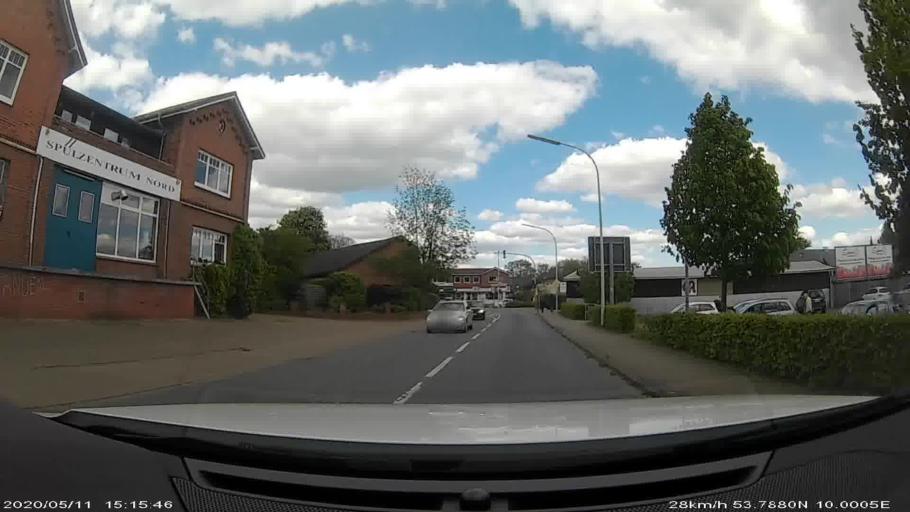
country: DE
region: Schleswig-Holstein
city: Henstedt-Ulzburg
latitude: 53.7899
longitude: 9.9870
